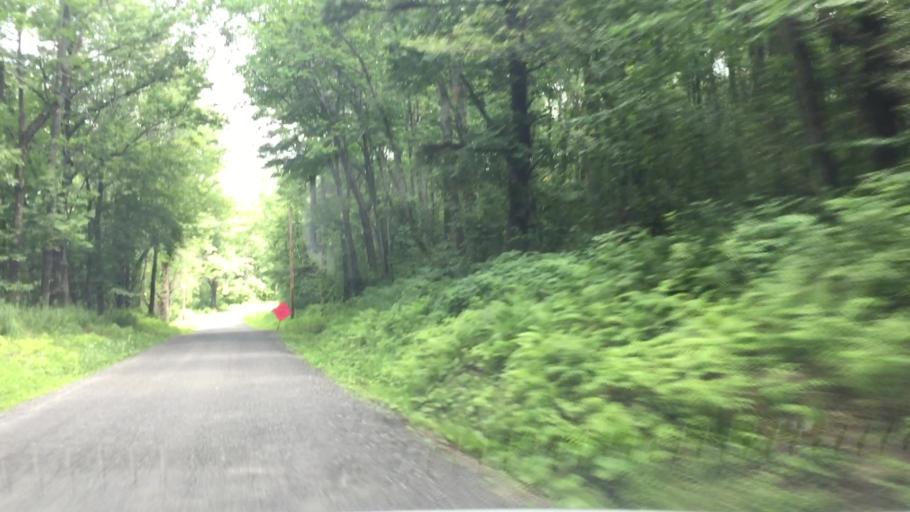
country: US
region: Massachusetts
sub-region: Berkshire County
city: Lee
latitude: 42.2739
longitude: -73.1861
